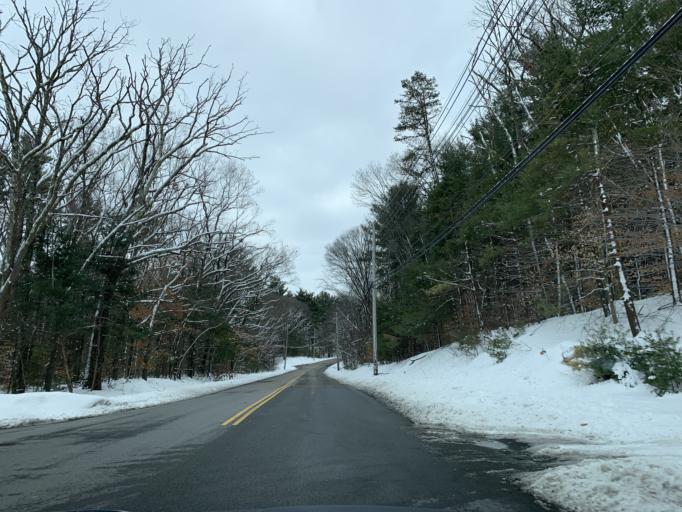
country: US
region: Massachusetts
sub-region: Norfolk County
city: Franklin
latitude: 42.0801
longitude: -71.4232
